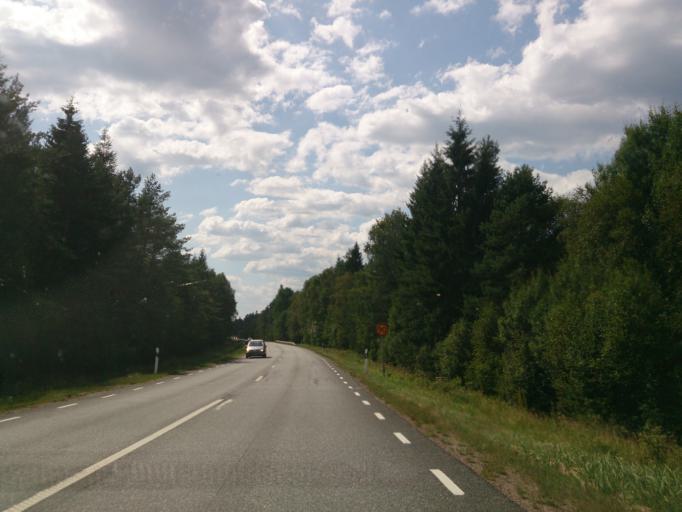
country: SE
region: Joenkoeping
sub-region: Varnamo Kommun
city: Bredaryd
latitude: 57.1740
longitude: 13.7150
